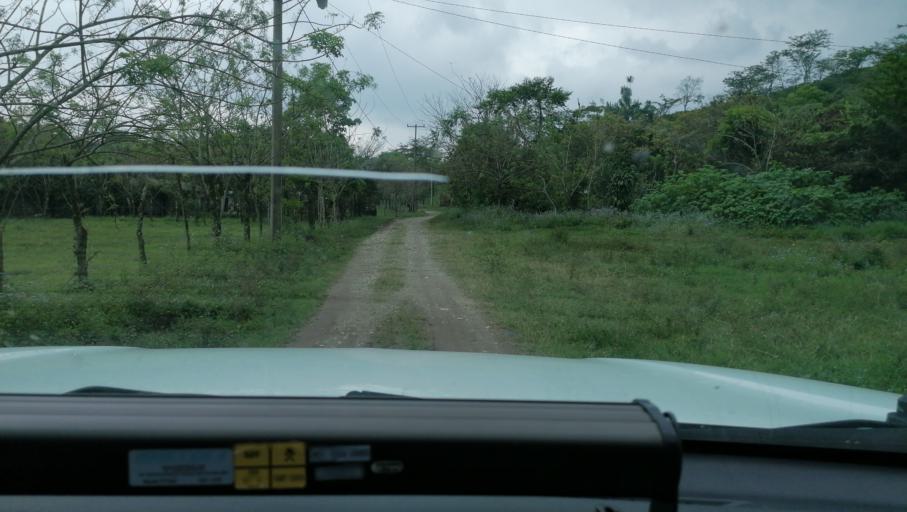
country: MX
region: Chiapas
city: Ixtacomitan
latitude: 17.3691
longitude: -93.1824
